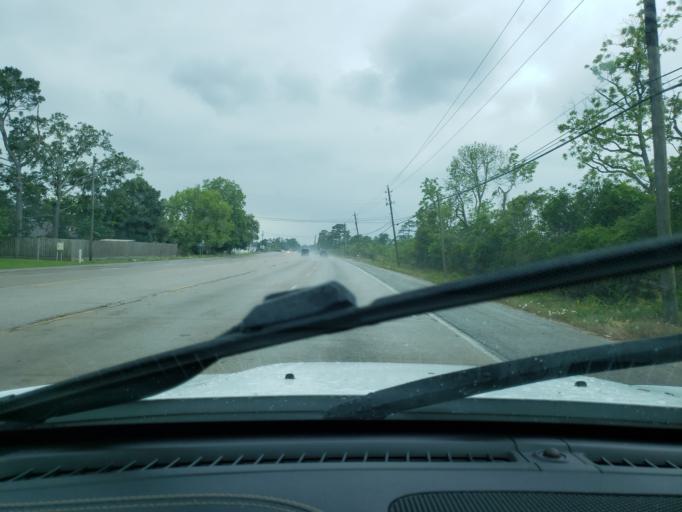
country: US
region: Texas
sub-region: Chambers County
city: Mont Belvieu
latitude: 29.7905
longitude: -94.9106
